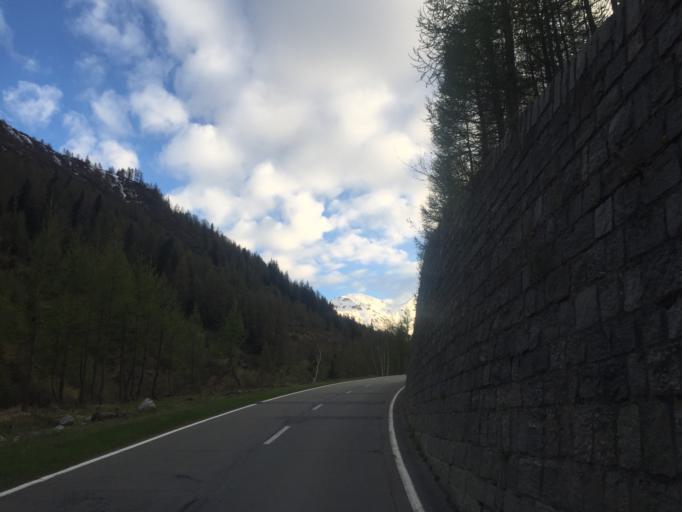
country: CH
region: Ticino
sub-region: Leventina District
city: Airolo
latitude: 46.4920
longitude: 8.4894
